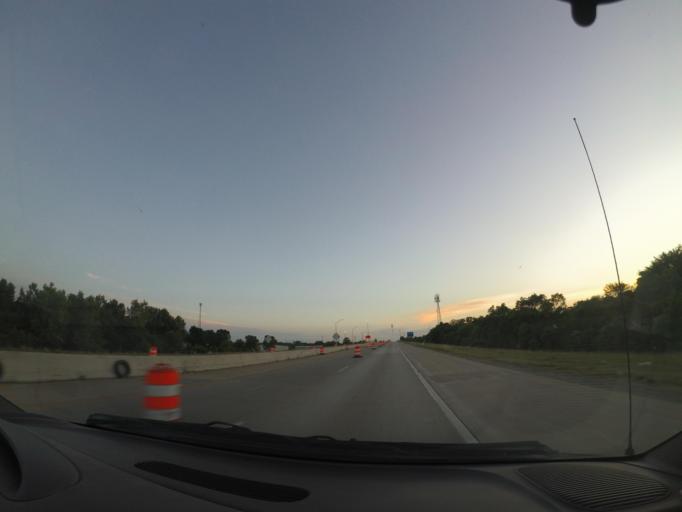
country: US
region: Indiana
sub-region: Elkhart County
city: Dunlap
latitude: 41.6548
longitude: -85.9354
